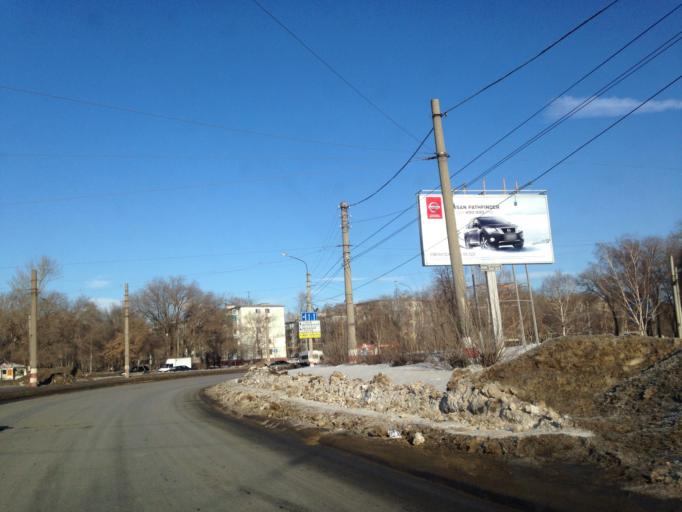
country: RU
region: Ulyanovsk
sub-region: Ulyanovskiy Rayon
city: Ulyanovsk
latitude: 54.2977
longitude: 48.3215
